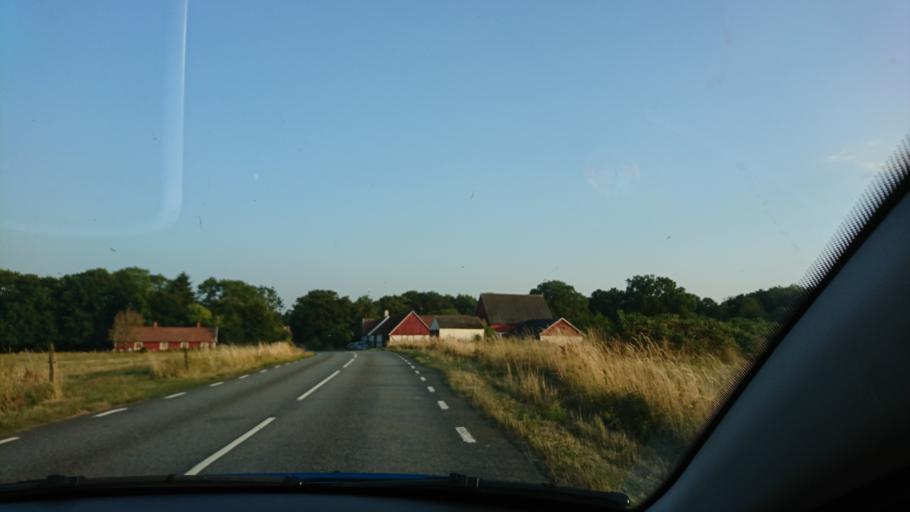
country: SE
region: Skane
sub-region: Simrishamns Kommun
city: Kivik
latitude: 55.7022
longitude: 14.1506
